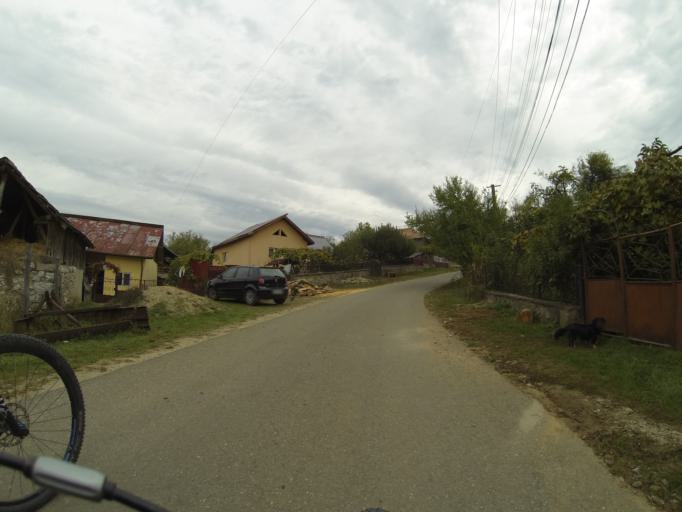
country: RO
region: Gorj
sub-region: Comuna Tismana
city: Sohodol
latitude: 45.0487
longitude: 22.8972
